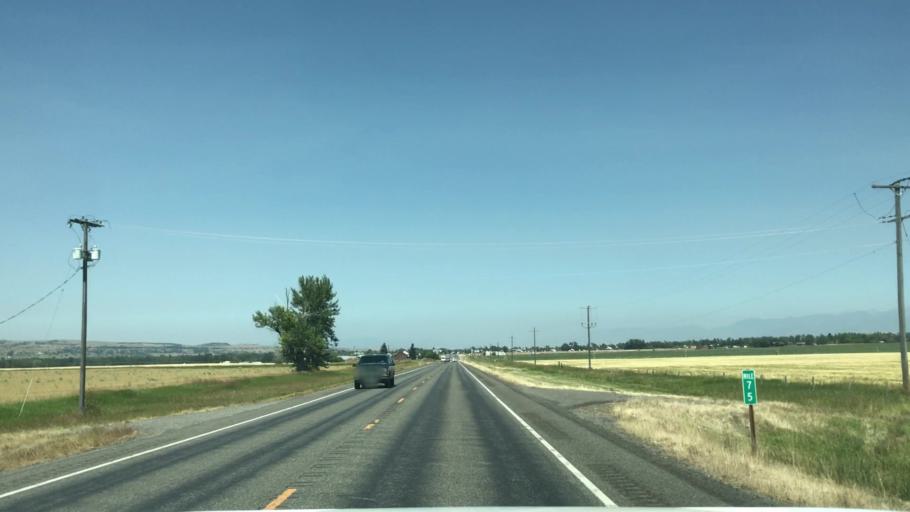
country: US
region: Montana
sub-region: Gallatin County
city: Four Corners
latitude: 45.5725
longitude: -111.1969
